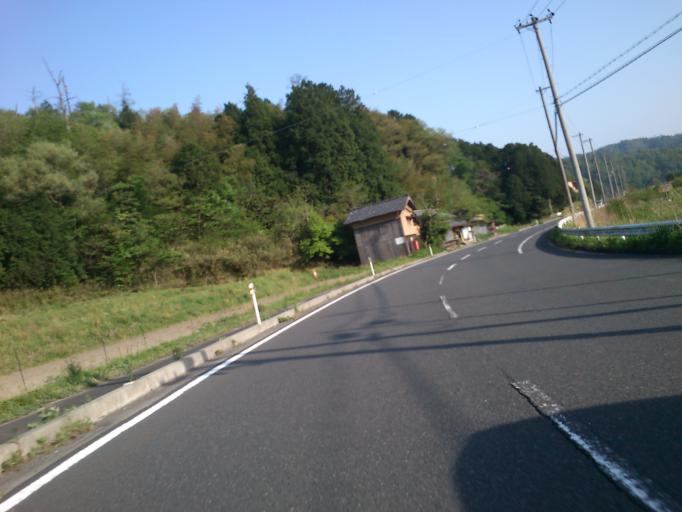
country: JP
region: Kyoto
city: Miyazu
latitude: 35.6051
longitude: 135.1380
